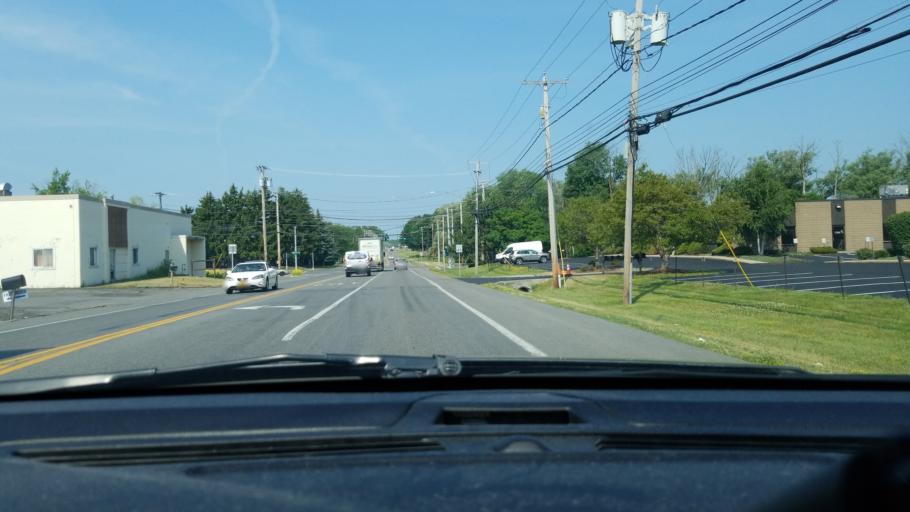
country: US
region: New York
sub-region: Onondaga County
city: Lyncourt
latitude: 43.0994
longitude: -76.0947
